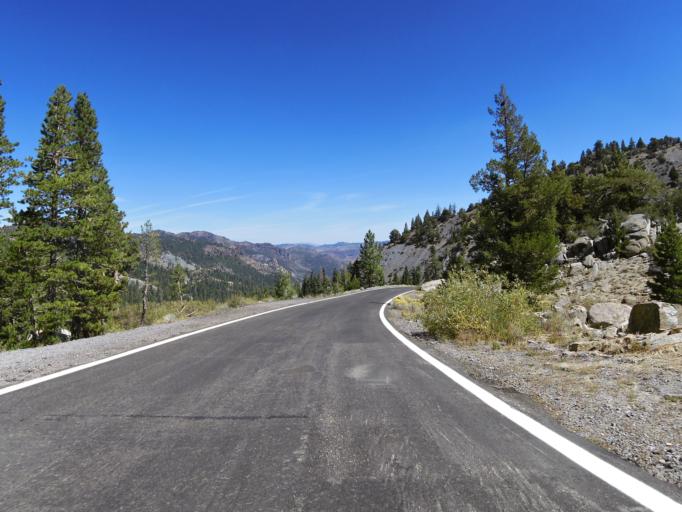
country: US
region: Nevada
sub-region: Douglas County
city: Gardnerville Ranchos
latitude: 38.5817
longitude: -119.8016
